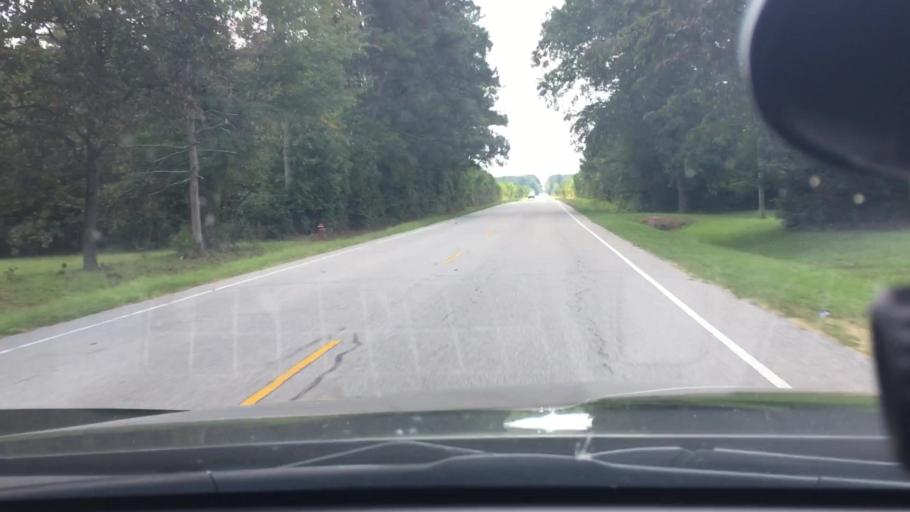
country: US
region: North Carolina
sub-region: Edgecombe County
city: Pinetops
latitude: 35.7754
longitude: -77.5775
